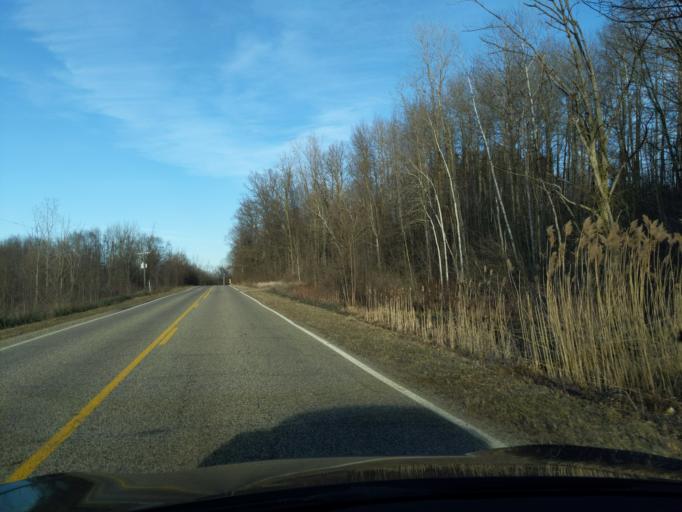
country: US
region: Michigan
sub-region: Ionia County
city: Ionia
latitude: 42.9618
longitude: -85.0980
